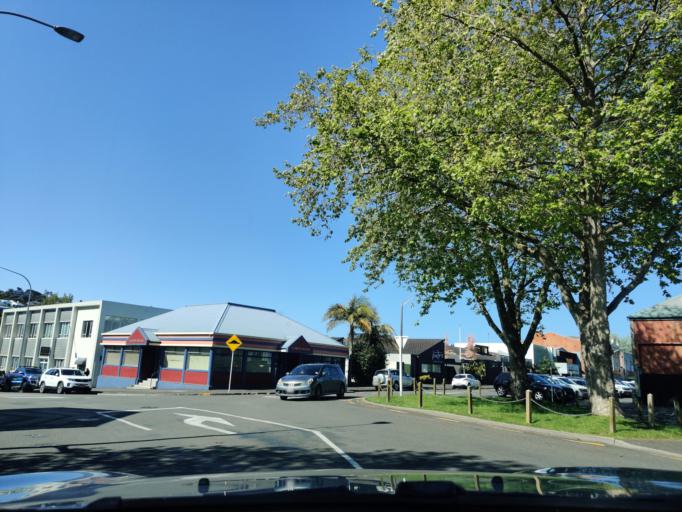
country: NZ
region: Manawatu-Wanganui
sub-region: Wanganui District
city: Wanganui
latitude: -39.9317
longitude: 175.0558
